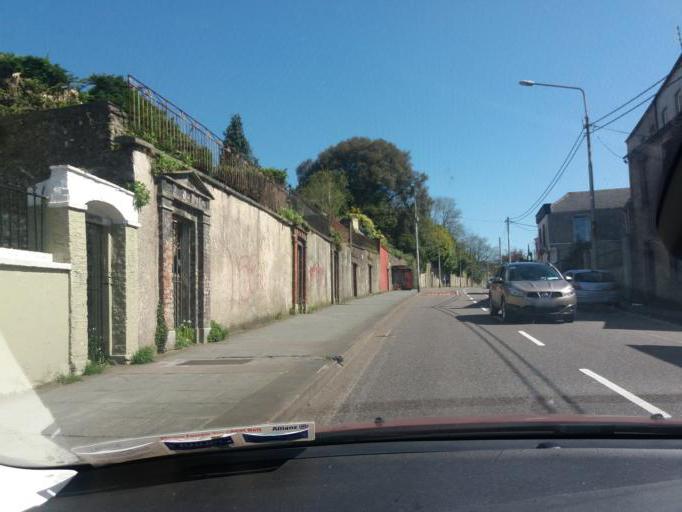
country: IE
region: Munster
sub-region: County Cork
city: Cork
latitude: 51.9028
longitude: -8.4609
